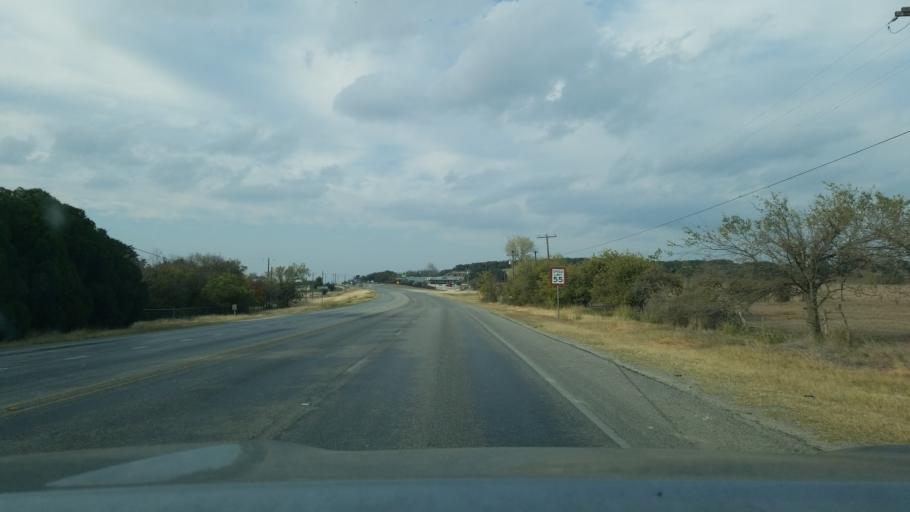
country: US
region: Texas
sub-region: Mills County
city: Goldthwaite
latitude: 31.4755
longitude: -98.5689
